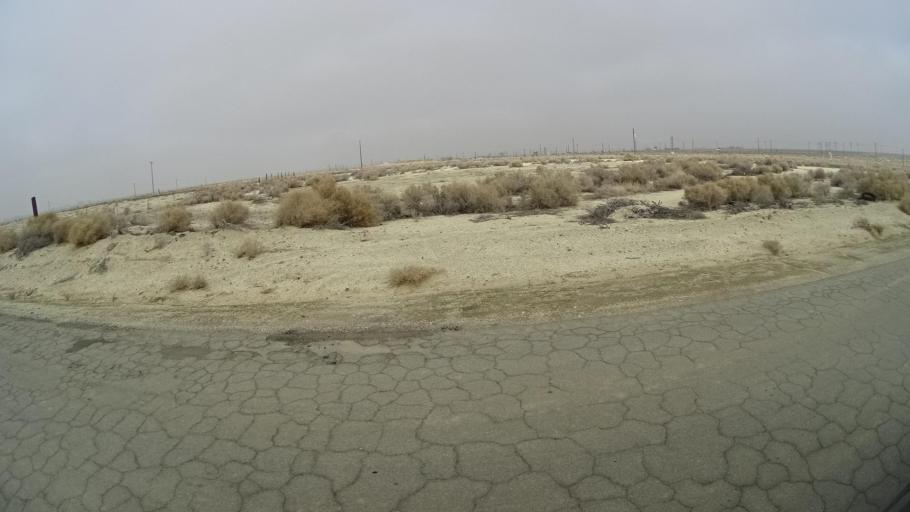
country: US
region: California
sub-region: Kern County
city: Maricopa
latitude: 35.0387
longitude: -119.3803
